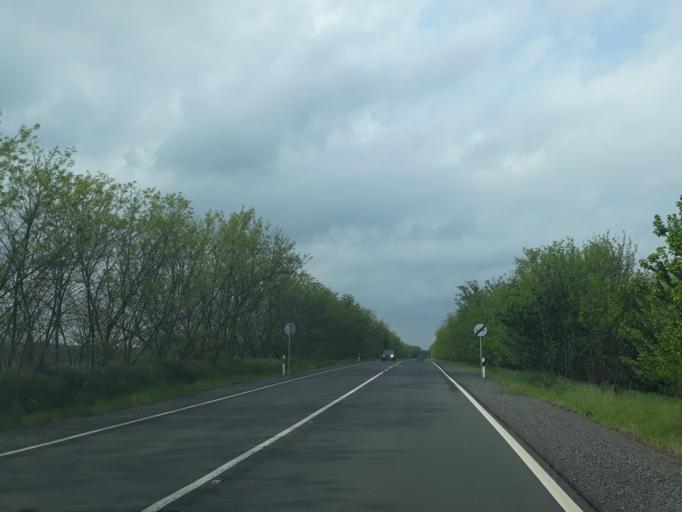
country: HU
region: Szabolcs-Szatmar-Bereg
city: Patroha
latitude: 48.1523
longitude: 22.0289
